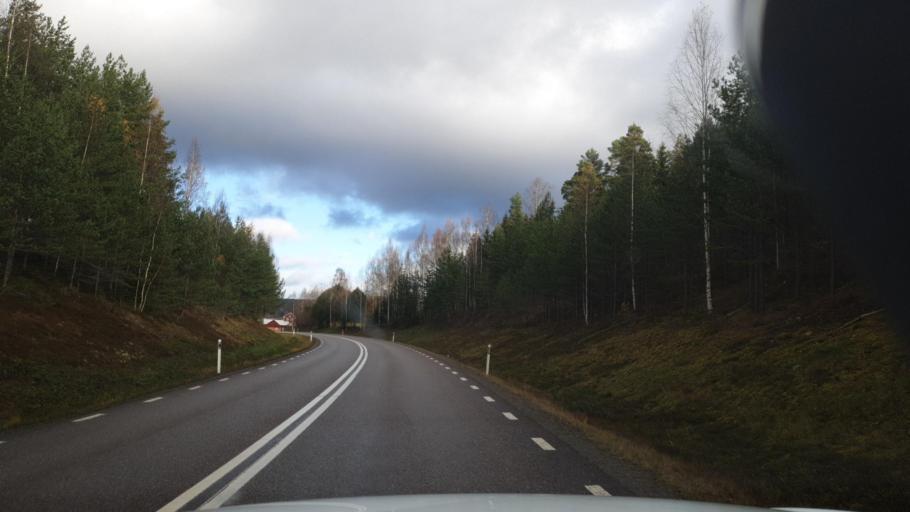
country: SE
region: Vaermland
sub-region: Arvika Kommun
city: Arvika
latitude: 59.4609
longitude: 12.7733
